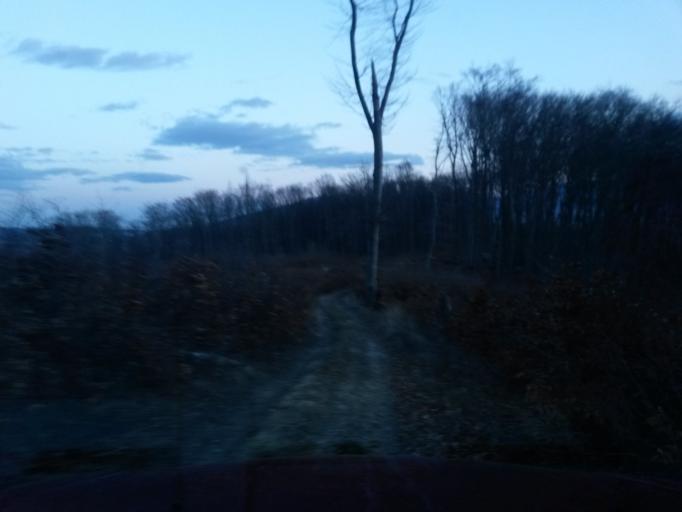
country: SK
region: Kosicky
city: Kosice
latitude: 48.7024
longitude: 21.3831
